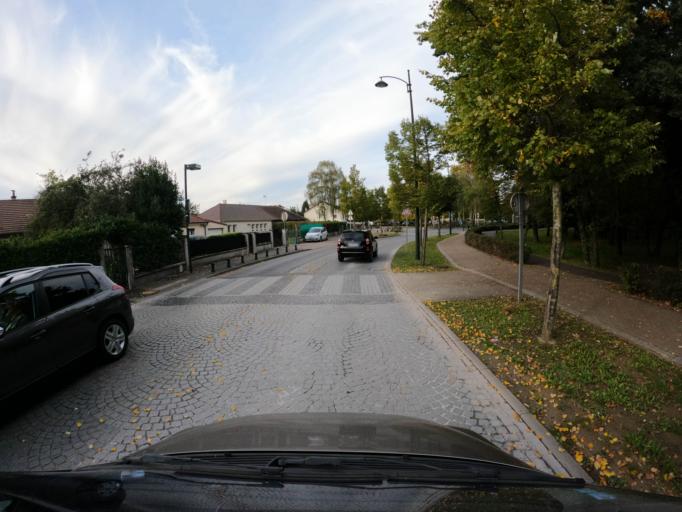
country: FR
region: Ile-de-France
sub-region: Departement de Seine-et-Marne
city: Pontault-Combault
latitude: 48.7948
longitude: 2.6110
